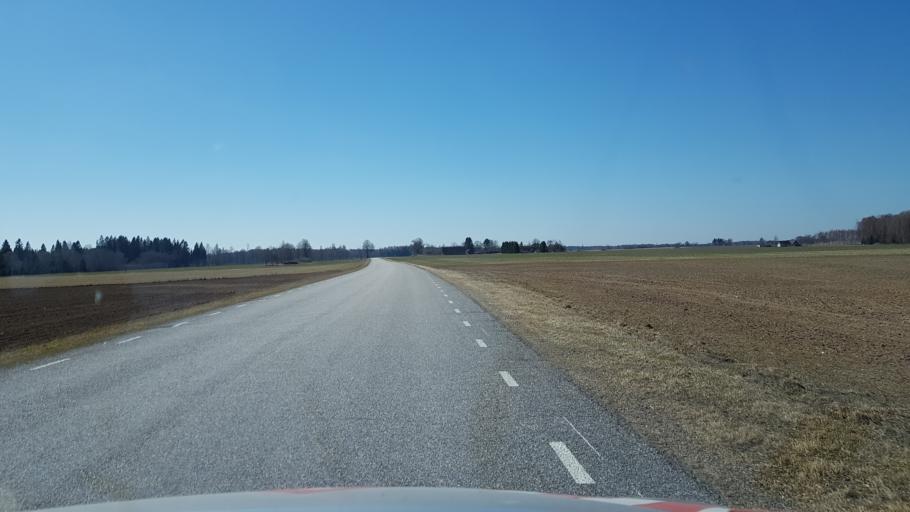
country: EE
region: Laeaene-Virumaa
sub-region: Vaeike-Maarja vald
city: Vaike-Maarja
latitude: 59.0634
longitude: 26.4750
